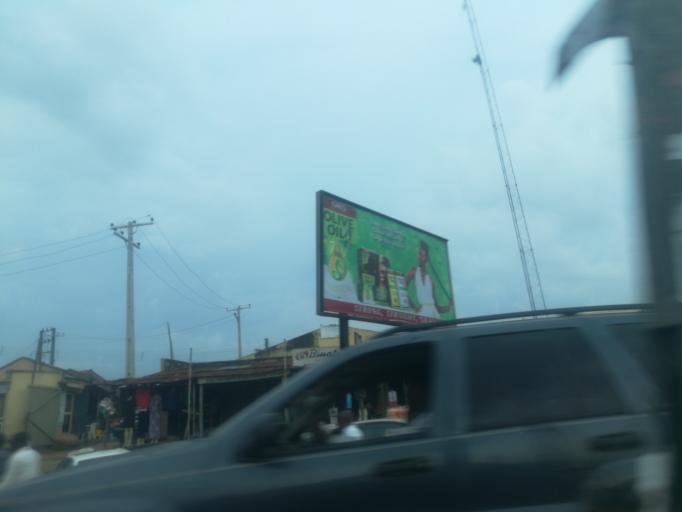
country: NG
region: Oyo
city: Ibadan
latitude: 7.4347
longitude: 3.9111
